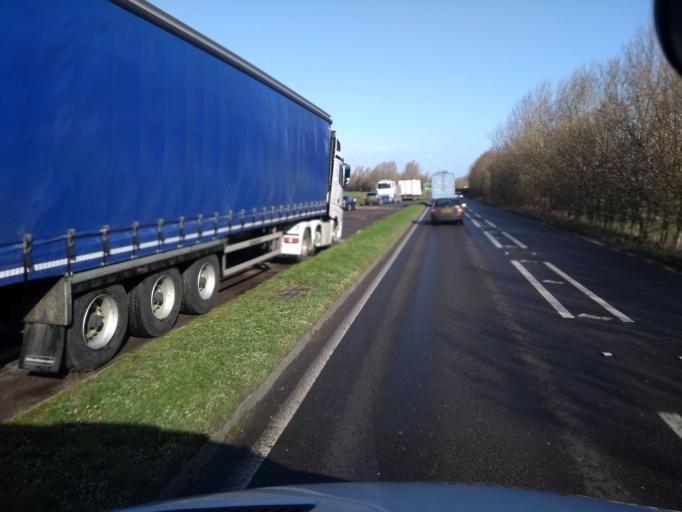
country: GB
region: England
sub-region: Somerset
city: Ilchester
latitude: 50.9946
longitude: -2.6798
